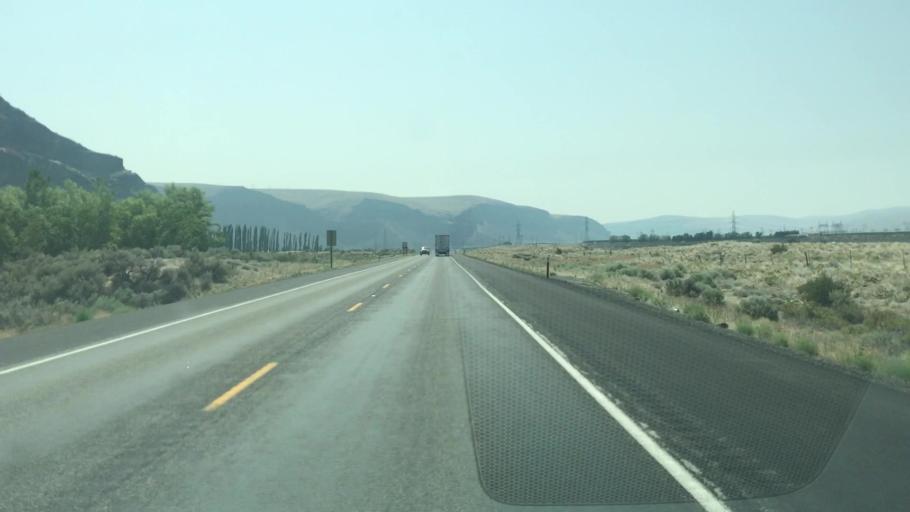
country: US
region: Washington
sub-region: Chelan County
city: South Wenatchee
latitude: 47.3129
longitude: -120.0712
